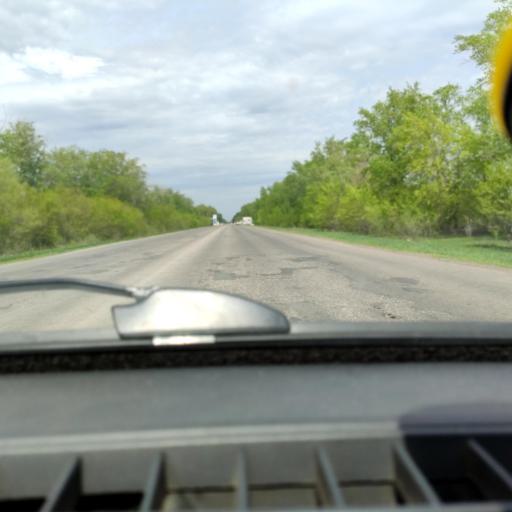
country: RU
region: Samara
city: Tol'yatti
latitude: 53.6163
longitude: 49.4134
